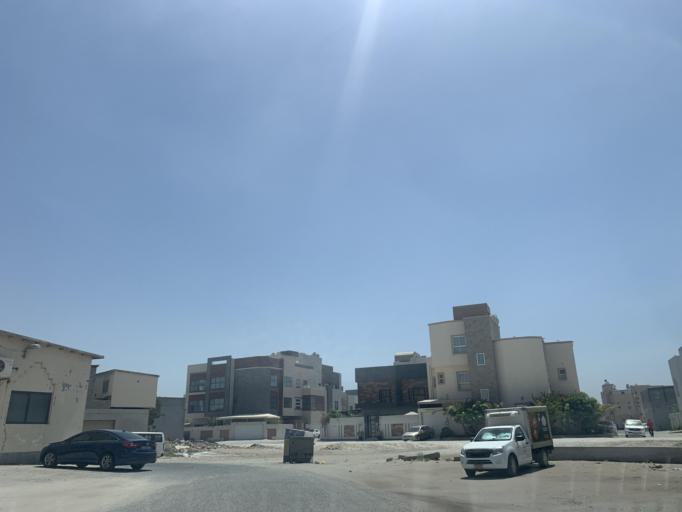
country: BH
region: Manama
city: Jidd Hafs
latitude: 26.2246
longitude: 50.5124
